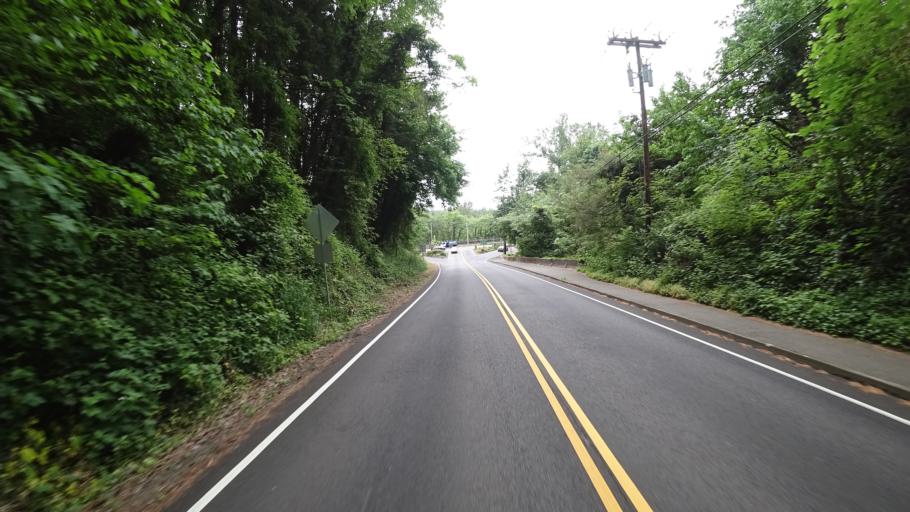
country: US
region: Oregon
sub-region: Clackamas County
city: Lake Oswego
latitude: 45.4250
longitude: -122.6616
